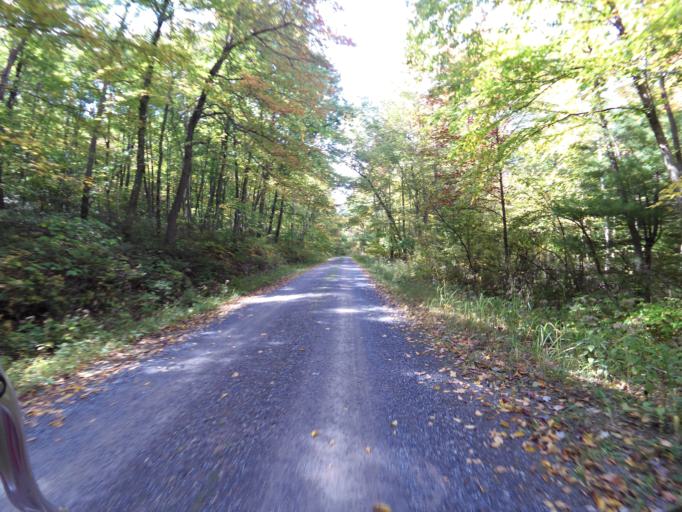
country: US
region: Pennsylvania
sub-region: Lycoming County
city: Jersey Shore
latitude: 41.0985
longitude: -77.1413
